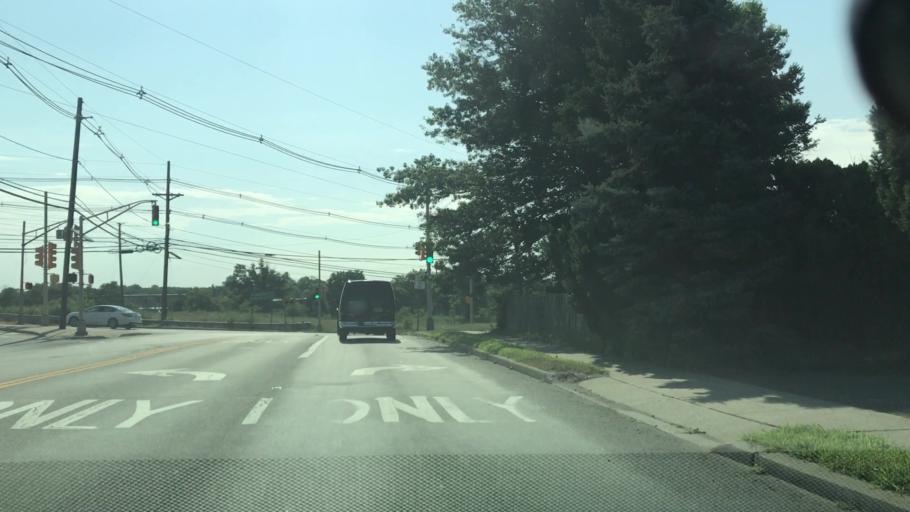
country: US
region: New Jersey
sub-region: Middlesex County
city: South Plainfield
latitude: 40.5594
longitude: -74.4185
